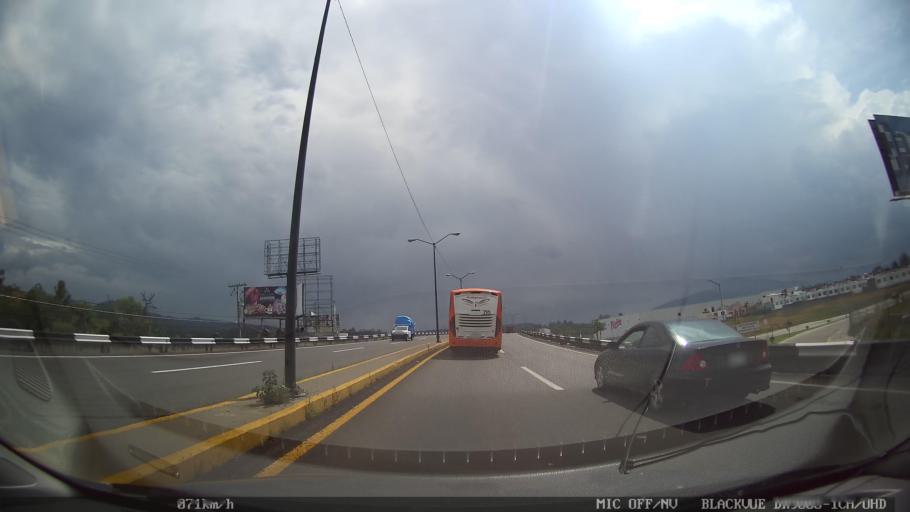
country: MX
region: Michoacan
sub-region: Morelia
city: Morelos
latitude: 19.6671
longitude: -101.2266
